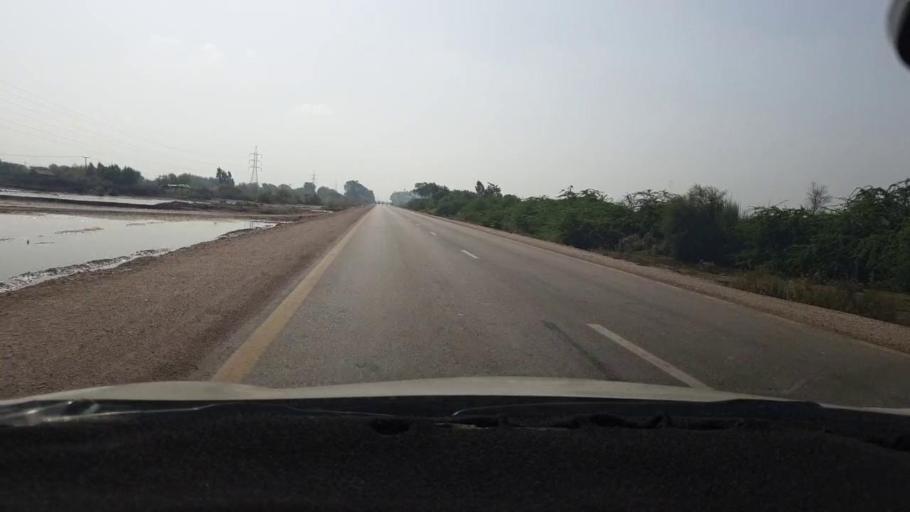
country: PK
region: Sindh
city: Jhol
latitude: 25.9075
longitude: 69.0164
